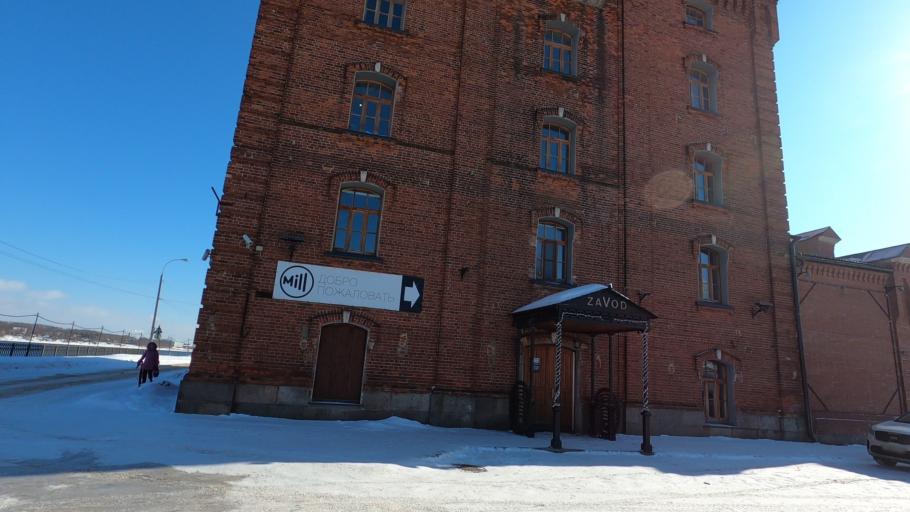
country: RU
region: Jaroslavl
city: Rybinsk
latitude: 58.0467
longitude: 38.8685
